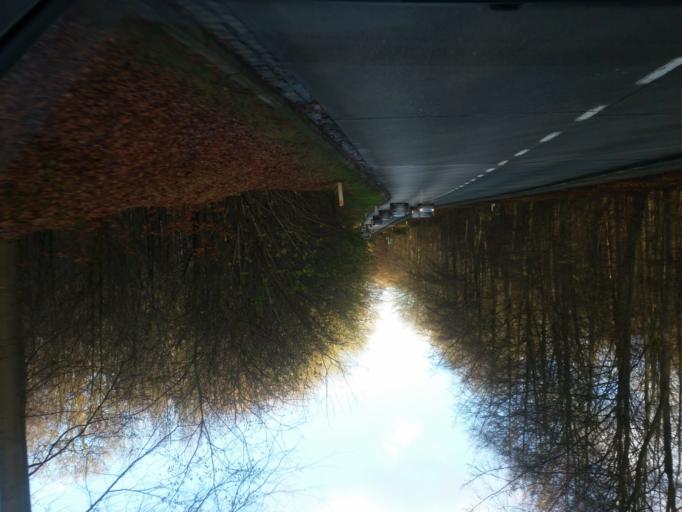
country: BE
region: Flanders
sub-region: Provincie Vlaams-Brabant
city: Hoeilaart
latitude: 50.7733
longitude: 4.4377
